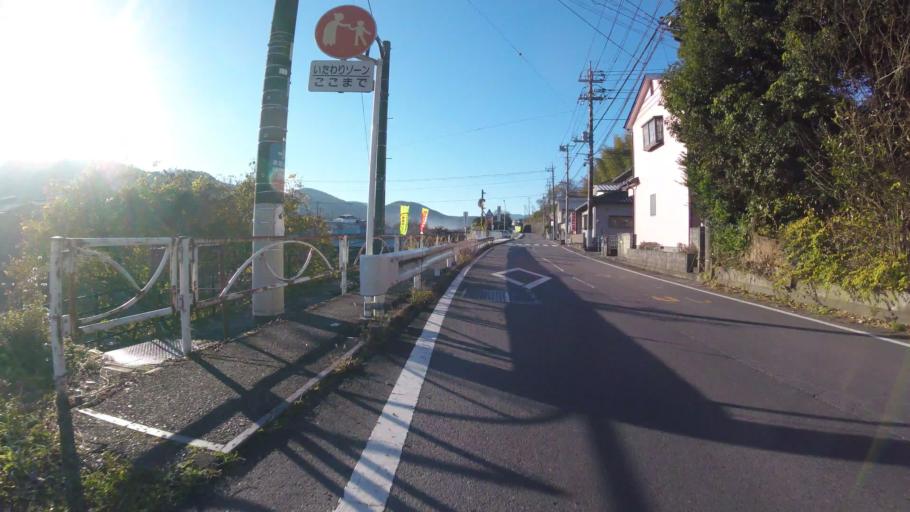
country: JP
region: Shizuoka
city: Ito
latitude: 34.9724
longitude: 138.9457
